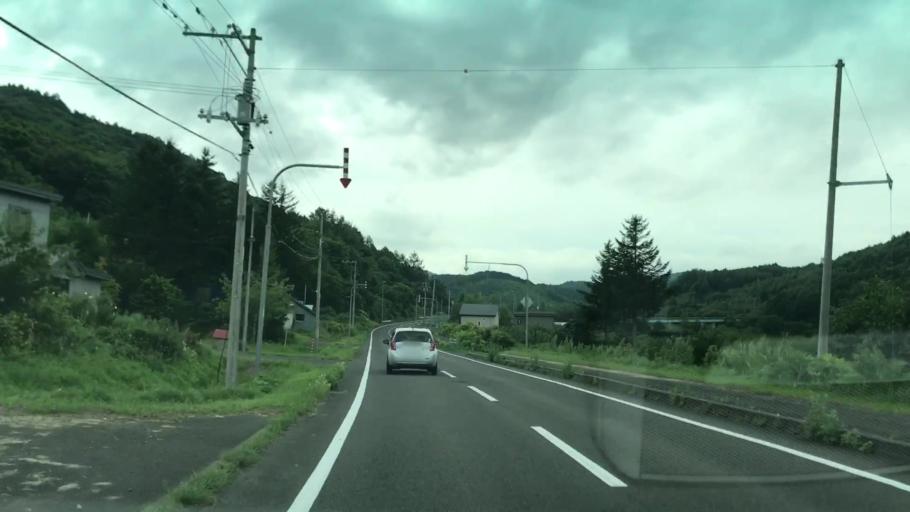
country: JP
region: Hokkaido
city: Yoichi
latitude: 43.1524
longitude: 140.8217
